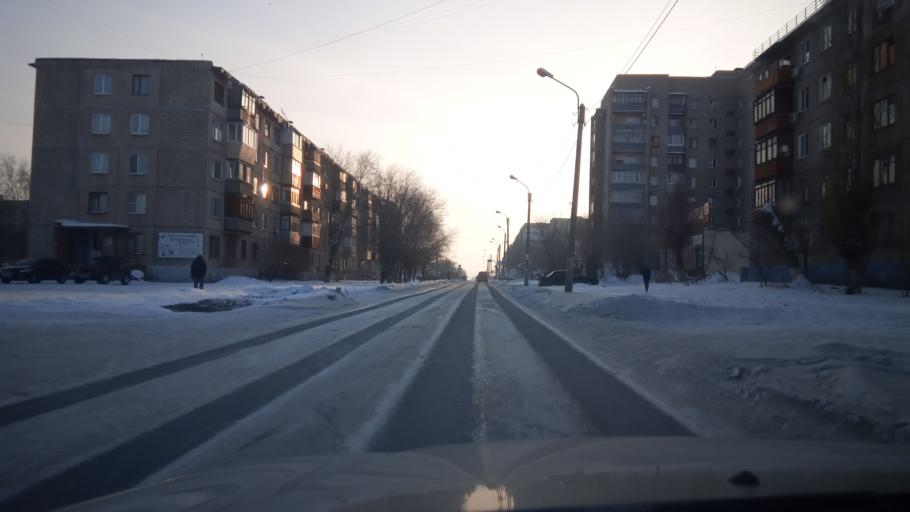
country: RU
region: Orenburg
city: Novotroitsk
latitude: 51.1870
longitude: 58.2792
